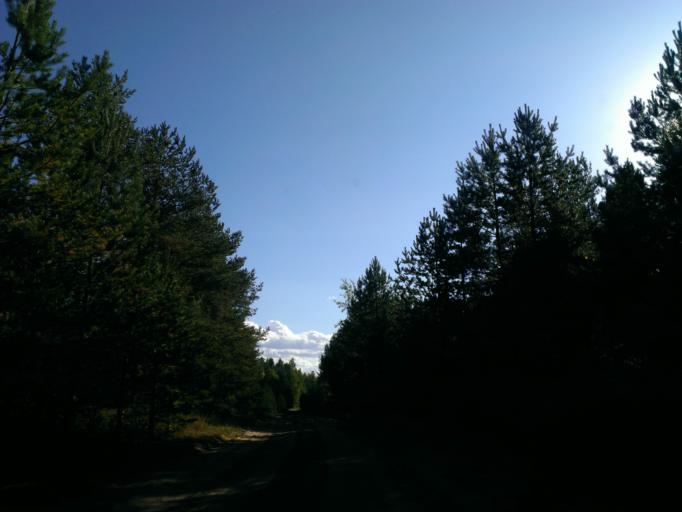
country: LV
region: Adazi
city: Adazi
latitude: 57.0607
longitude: 24.2606
